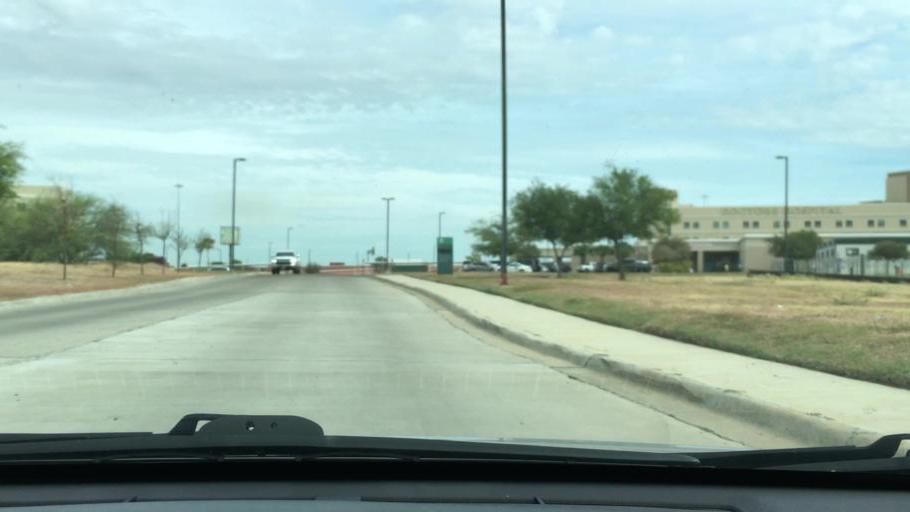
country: US
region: Texas
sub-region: Webb County
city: Laredo
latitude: 27.6048
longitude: -99.4790
